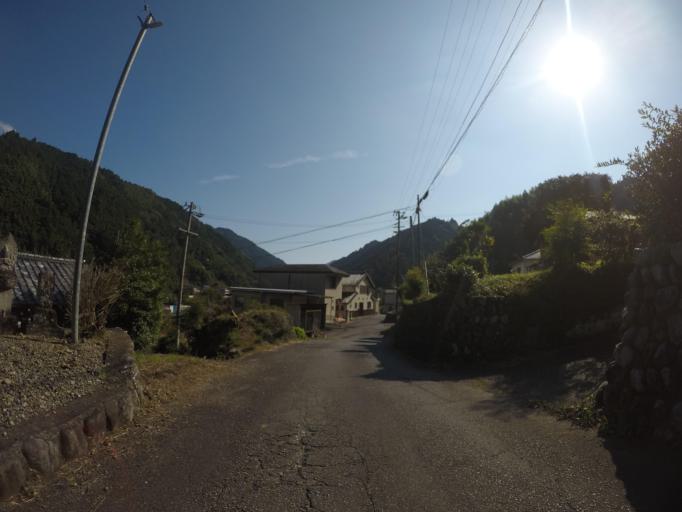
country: JP
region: Shizuoka
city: Fujinomiya
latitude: 35.1205
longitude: 138.4785
